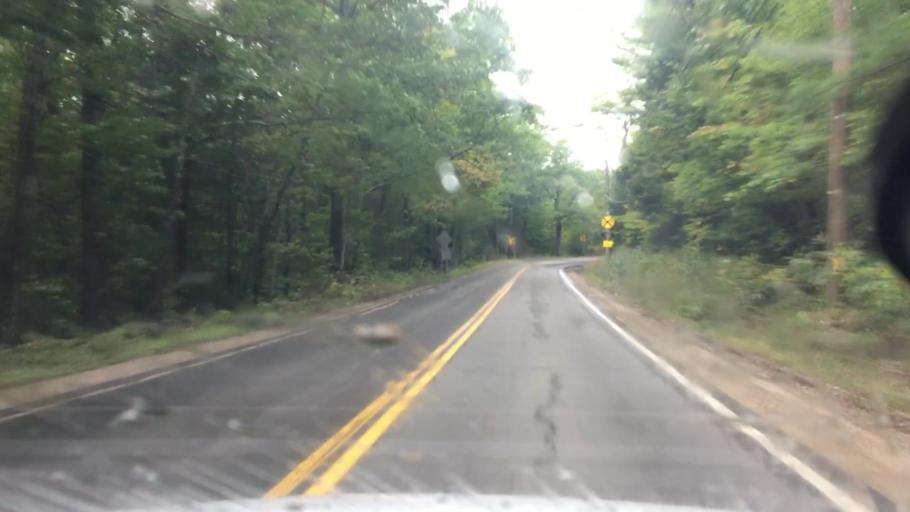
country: US
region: New Hampshire
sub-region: Carroll County
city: Wakefield
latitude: 43.5821
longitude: -71.0153
